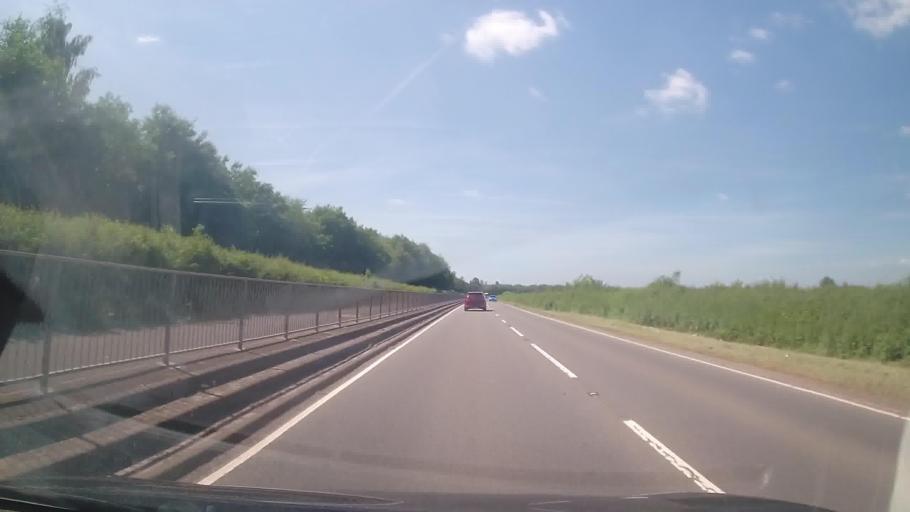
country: GB
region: England
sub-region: Herefordshire
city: Kimbolton
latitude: 52.2423
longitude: -2.7147
